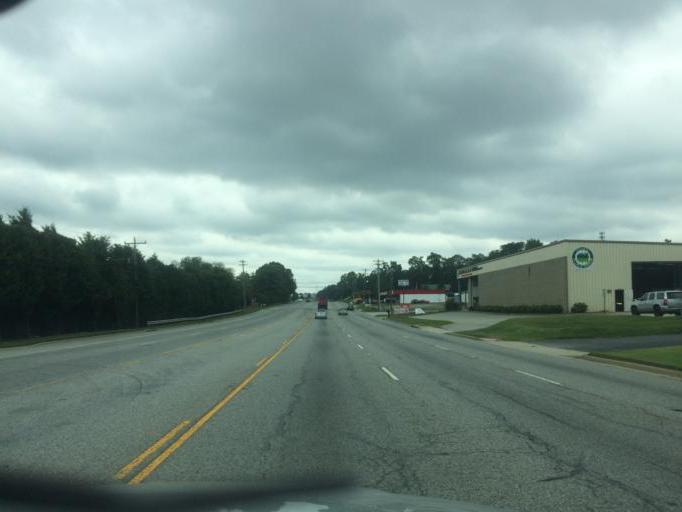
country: US
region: South Carolina
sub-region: Greenville County
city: Greer
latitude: 34.8948
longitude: -82.2342
